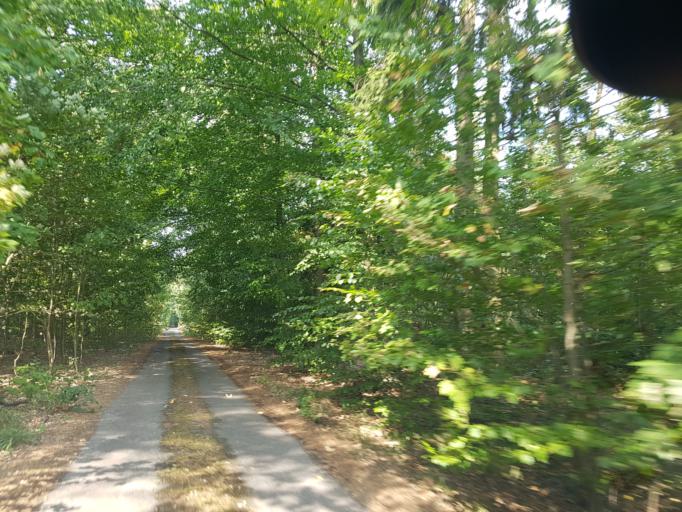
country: DE
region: Brandenburg
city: Gorzke
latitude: 52.0602
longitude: 12.2737
